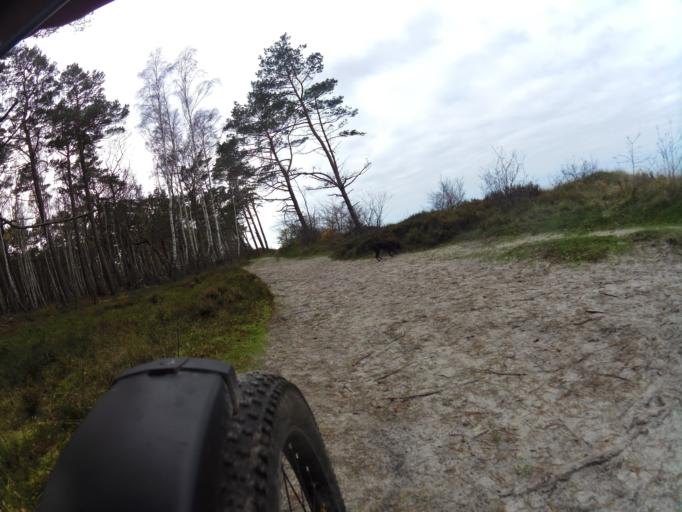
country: PL
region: Pomeranian Voivodeship
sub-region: Powiat wejherowski
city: Choczewo
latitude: 54.8098
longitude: 17.8264
